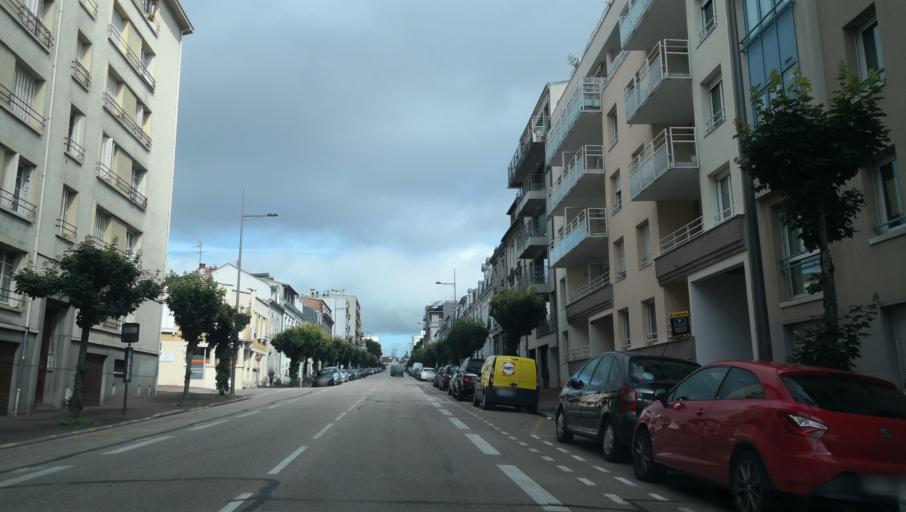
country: FR
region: Limousin
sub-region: Departement de la Haute-Vienne
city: Limoges
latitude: 45.8380
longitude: 1.2642
